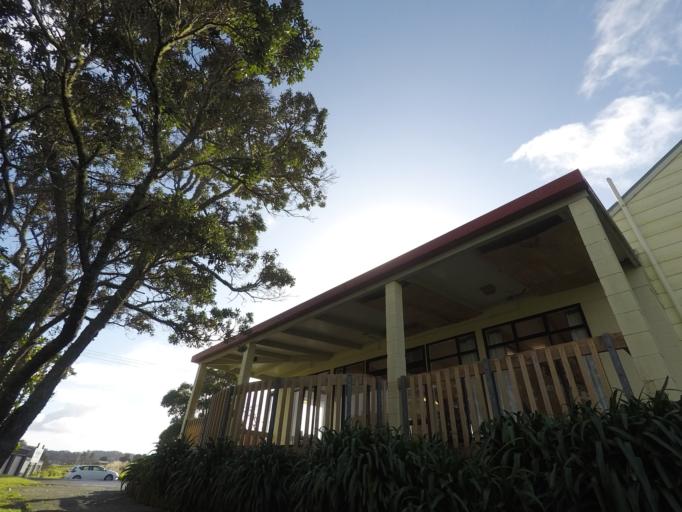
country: NZ
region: Auckland
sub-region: Auckland
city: Warkworth
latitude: -36.4212
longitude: 174.7226
